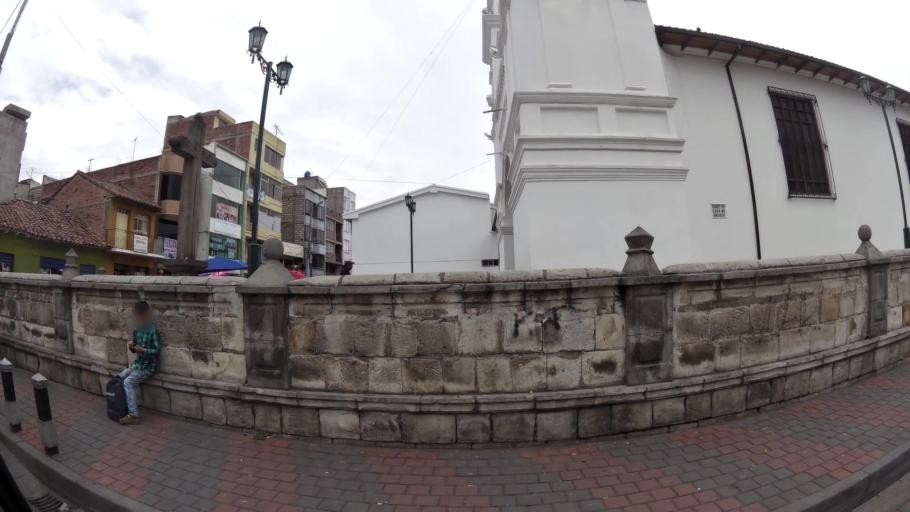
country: EC
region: Cotopaxi
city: San Miguel de Salcedo
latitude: -1.0433
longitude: -78.5905
